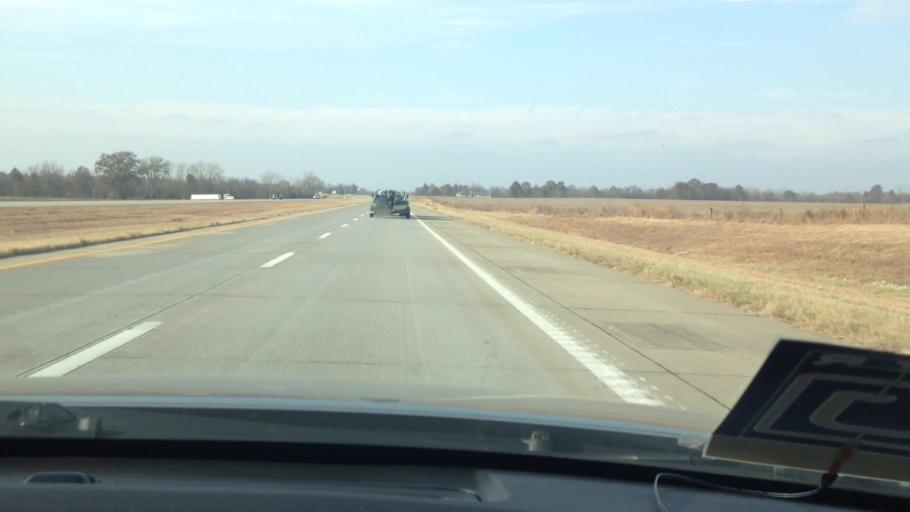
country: US
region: Missouri
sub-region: Henry County
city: Clinton
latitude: 38.4486
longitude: -93.9584
